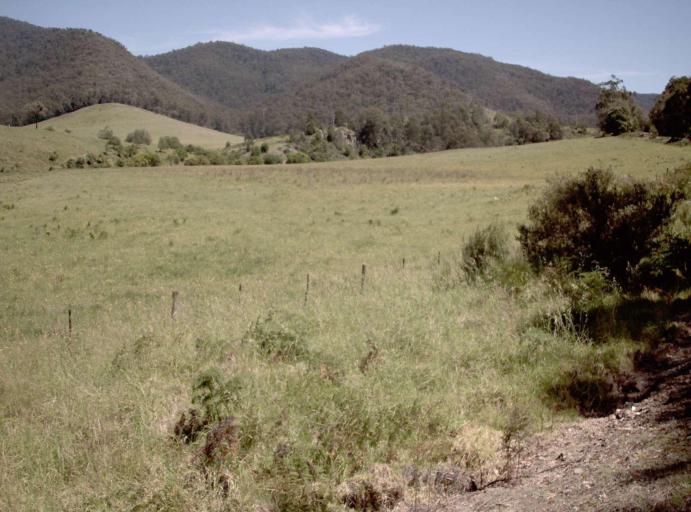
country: AU
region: Victoria
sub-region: East Gippsland
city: Lakes Entrance
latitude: -37.3906
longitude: 148.2190
